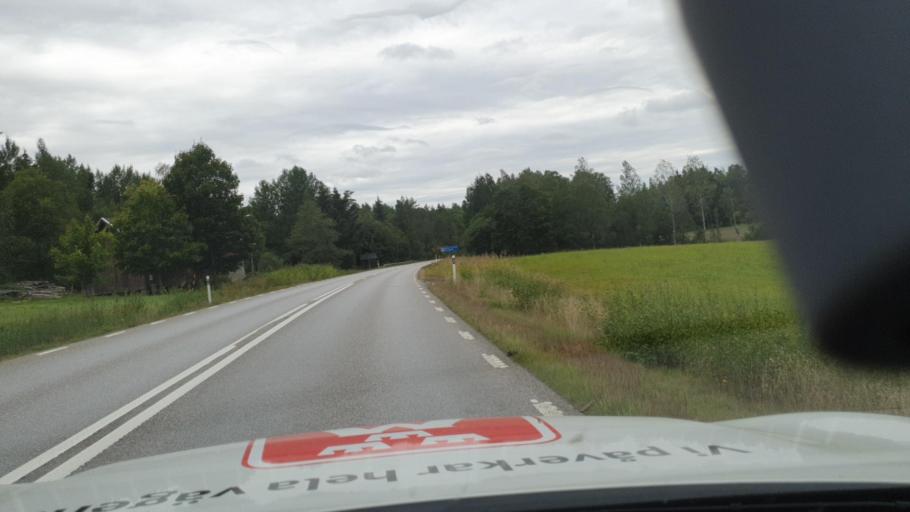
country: SE
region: Vaestra Goetaland
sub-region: Bengtsfors Kommun
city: Dals Langed
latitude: 58.7677
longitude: 12.2210
